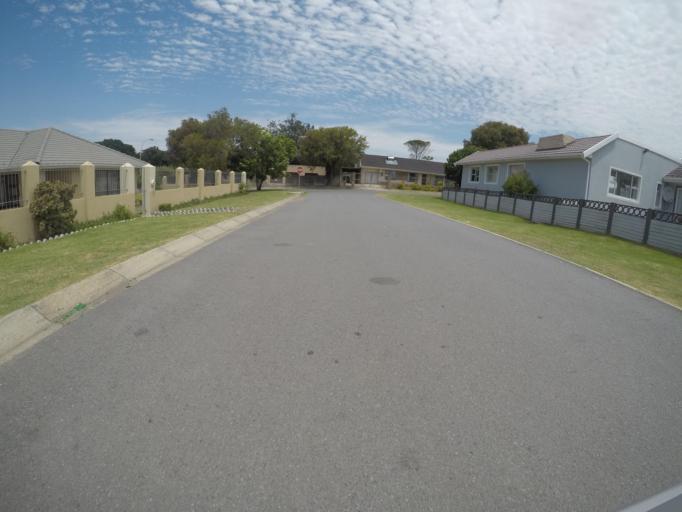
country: ZA
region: Eastern Cape
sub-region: Buffalo City Metropolitan Municipality
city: East London
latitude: -32.9838
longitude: 27.8613
